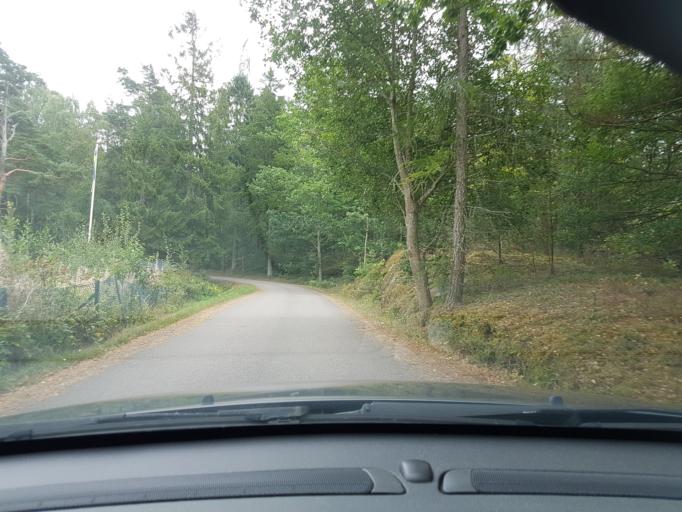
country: SE
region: Vaestra Goetaland
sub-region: Ale Kommun
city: Surte
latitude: 57.8291
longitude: 12.0254
